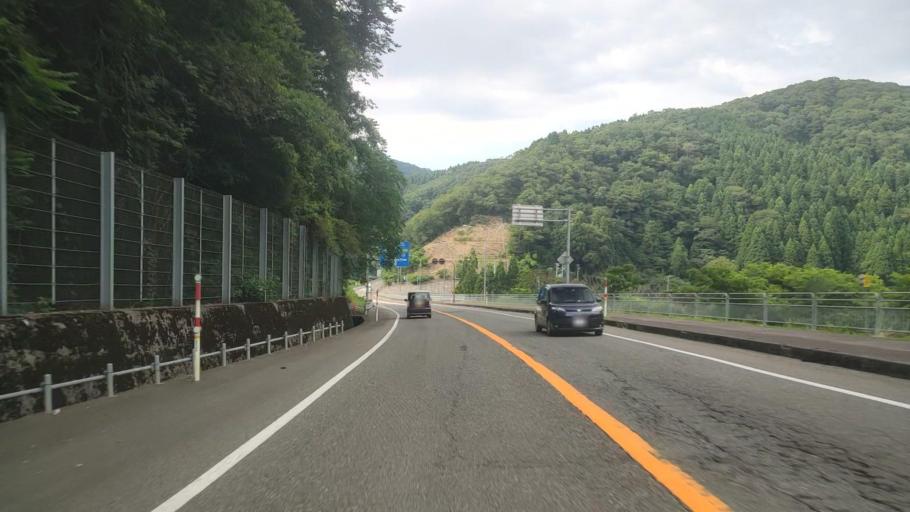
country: JP
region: Fukui
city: Takefu
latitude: 35.8154
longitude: 136.1017
